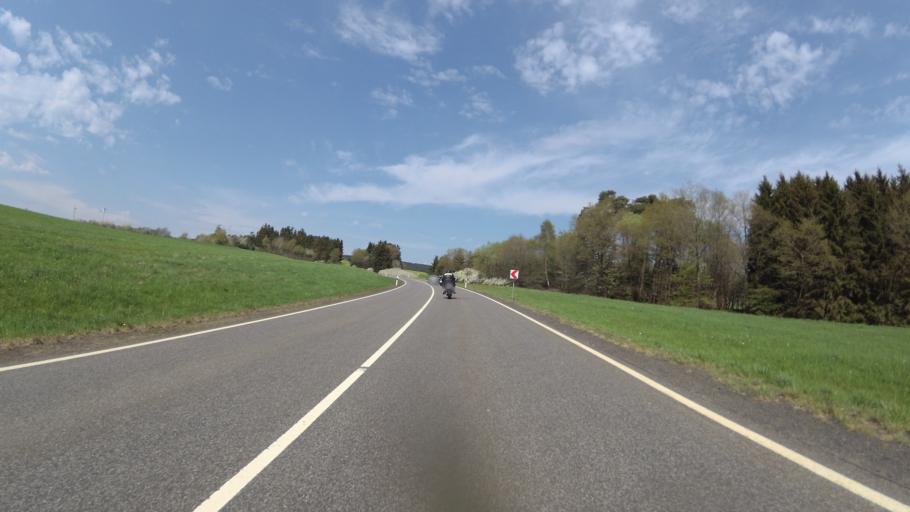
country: DE
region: Rheinland-Pfalz
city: Horschhausen
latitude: 50.2509
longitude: 6.9288
